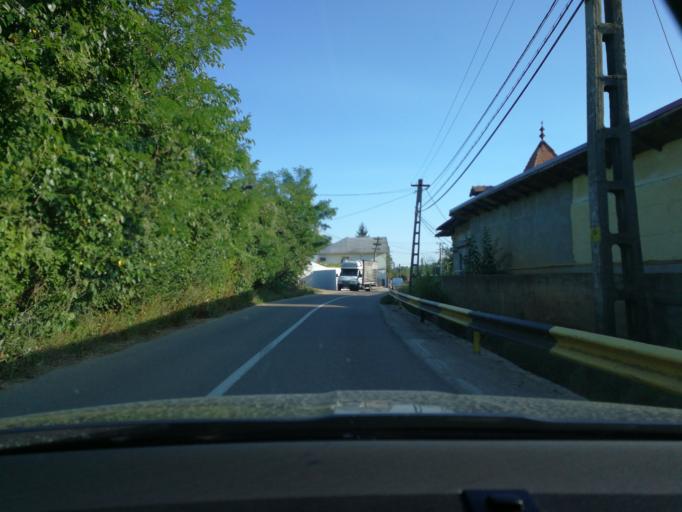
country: RO
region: Prahova
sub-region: Comuna Ceptura
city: Ceptura de Jos
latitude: 45.0289
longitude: 26.3217
